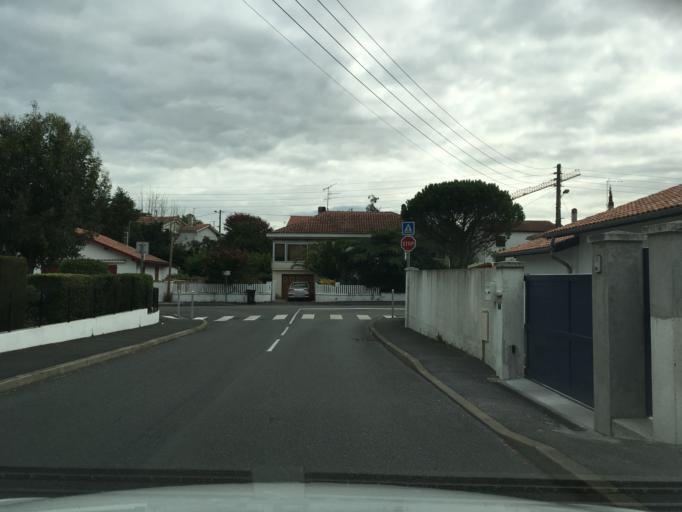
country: FR
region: Aquitaine
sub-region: Departement des Pyrenees-Atlantiques
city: Anglet
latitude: 43.5004
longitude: -1.5073
